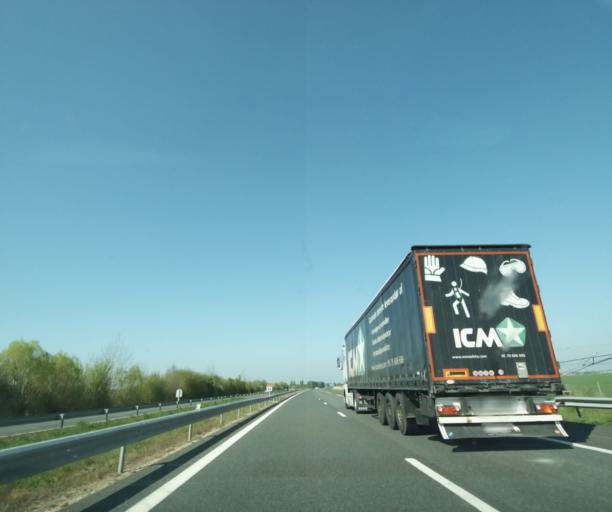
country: FR
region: Centre
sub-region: Departement du Loiret
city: Vimory
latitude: 47.9523
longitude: 2.6731
